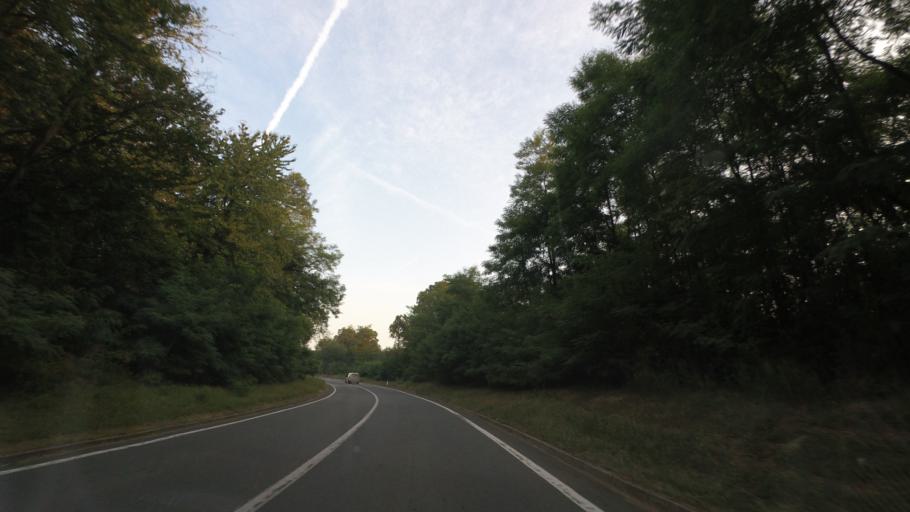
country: HR
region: Brodsko-Posavska
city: Nova Gradiska
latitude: 45.2660
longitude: 17.4101
